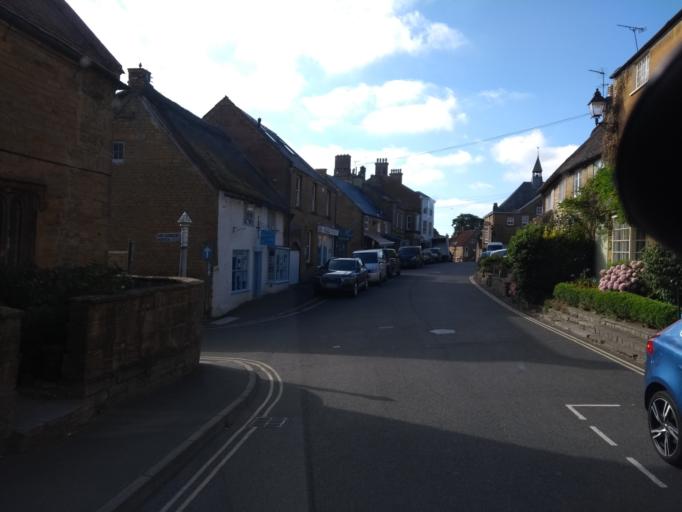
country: GB
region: England
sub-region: Somerset
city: South Petherton
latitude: 50.9497
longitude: -2.8098
